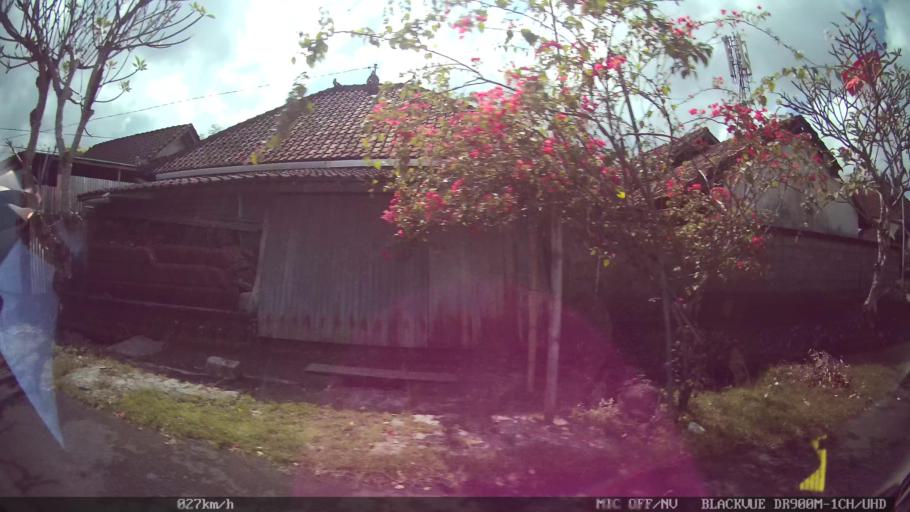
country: ID
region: Bali
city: Banjar Batur
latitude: -8.5971
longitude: 115.2096
